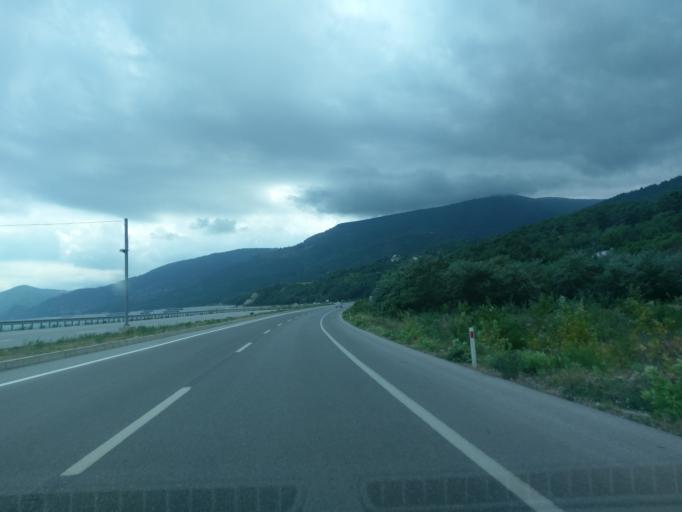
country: TR
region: Sinop
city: Gerze
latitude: 41.7801
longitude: 35.2021
